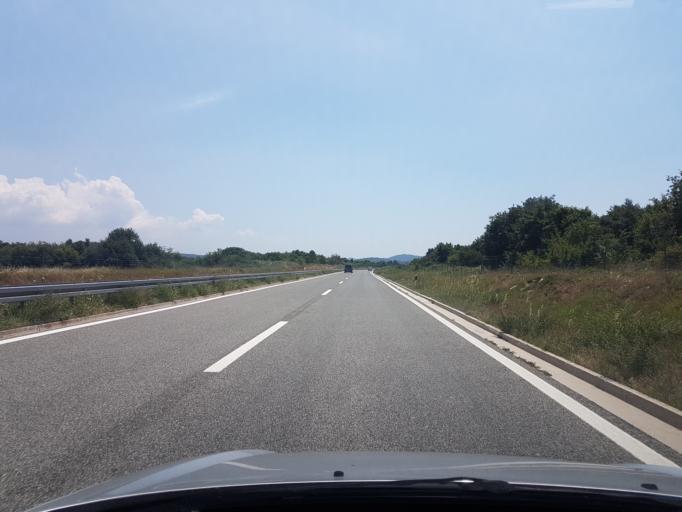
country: HR
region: Istarska
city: Vrsar
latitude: 45.1800
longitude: 13.7333
